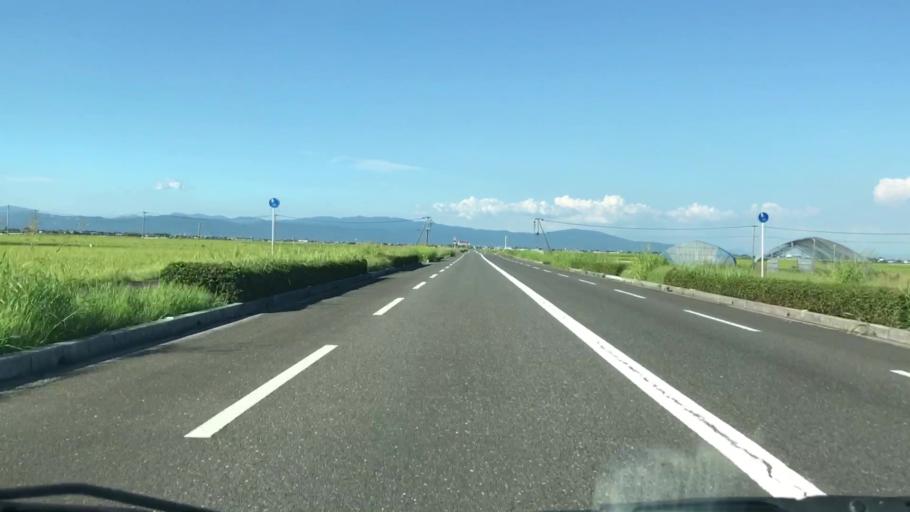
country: JP
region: Saga Prefecture
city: Okawa
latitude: 33.1701
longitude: 130.2944
